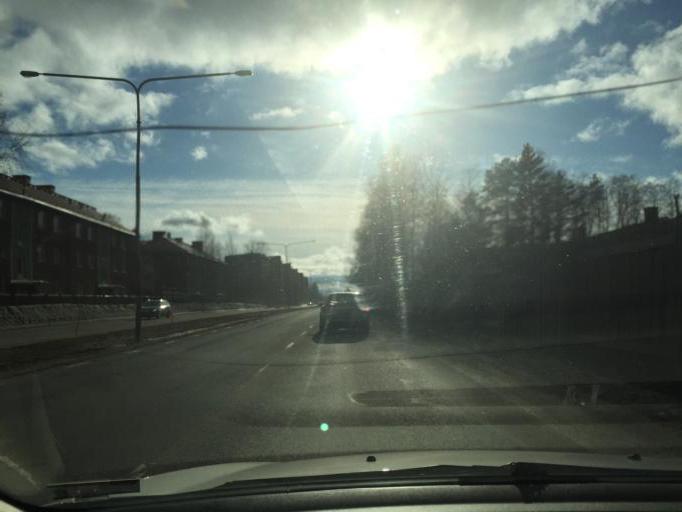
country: SE
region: Norrbotten
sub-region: Lulea Kommun
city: Lulea
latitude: 65.5829
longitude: 22.2062
